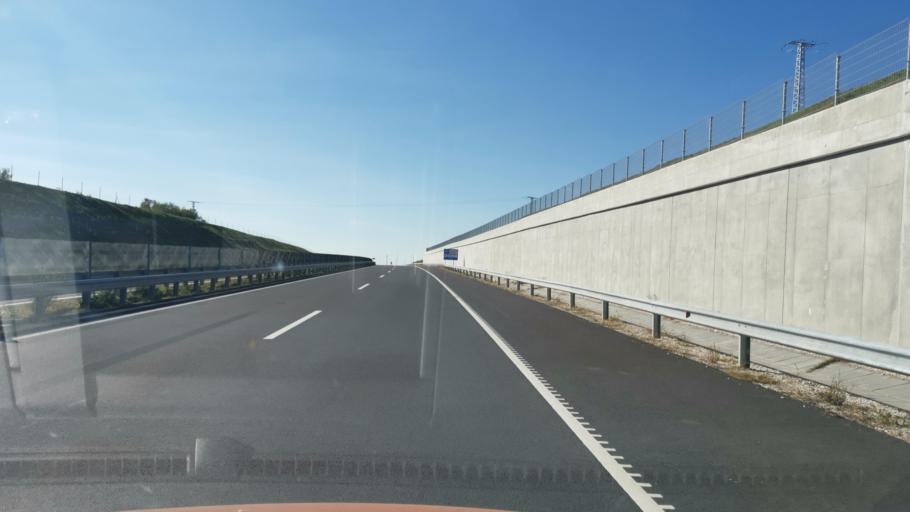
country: HU
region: Borsod-Abauj-Zemplen
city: Encs
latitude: 48.3856
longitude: 21.1498
